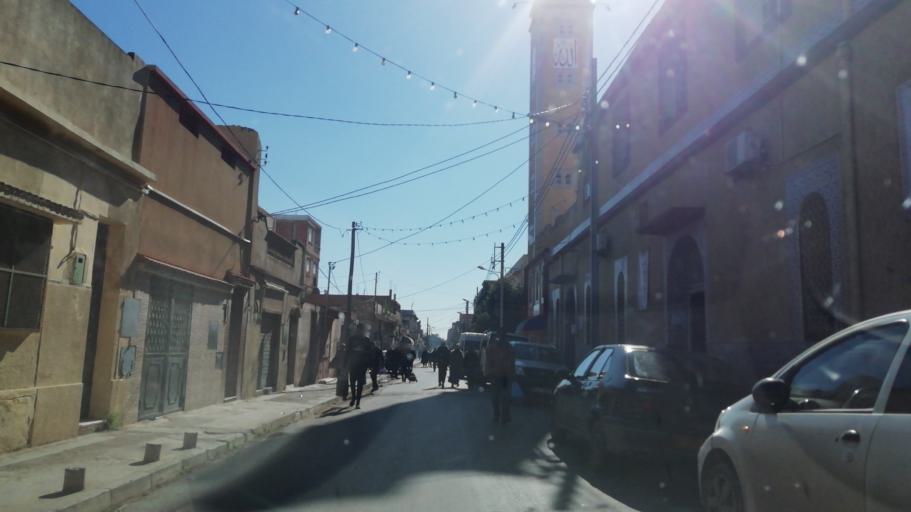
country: DZ
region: Oran
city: Oran
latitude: 35.6886
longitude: -0.6406
